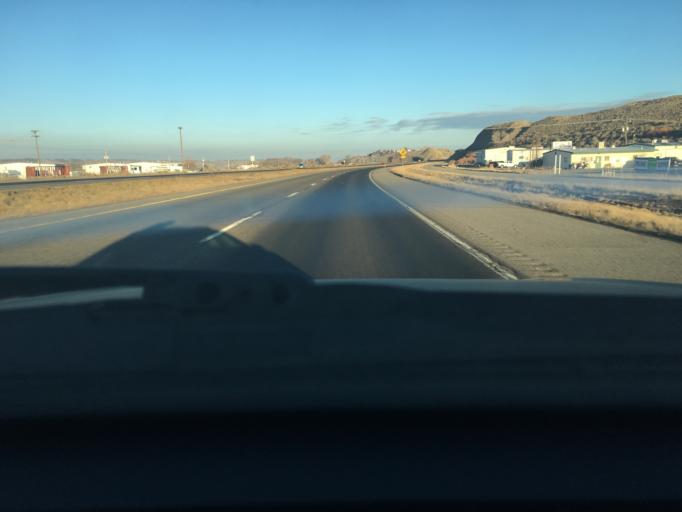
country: US
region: Colorado
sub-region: Montrose County
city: Montrose
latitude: 38.5289
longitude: -107.9339
